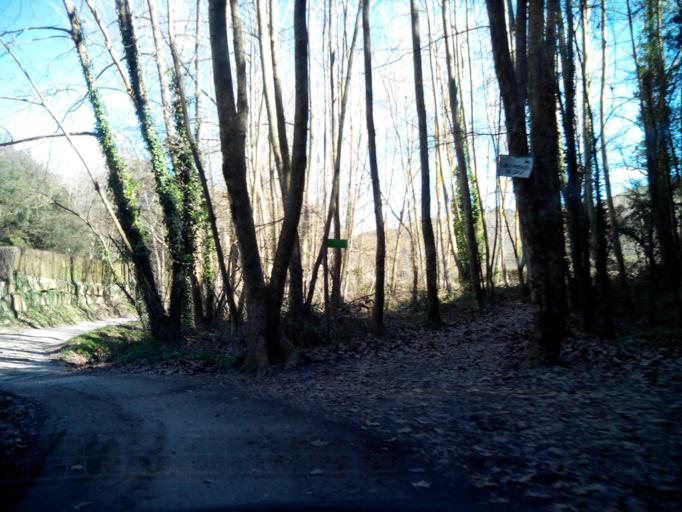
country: ES
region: Catalonia
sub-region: Provincia de Barcelona
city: Sant Andreu de Llavaneres
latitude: 41.6081
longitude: 2.4656
